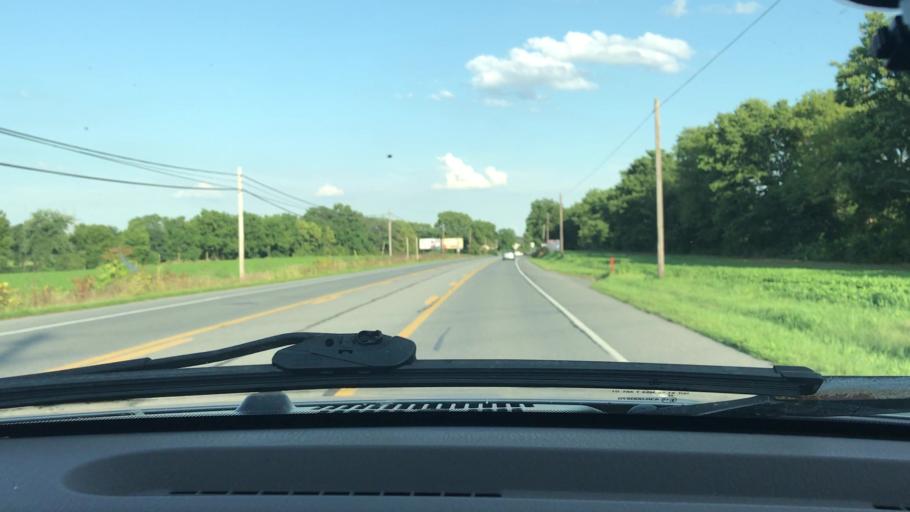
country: US
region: Pennsylvania
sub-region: Lancaster County
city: Rheems
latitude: 40.1265
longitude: -76.5505
